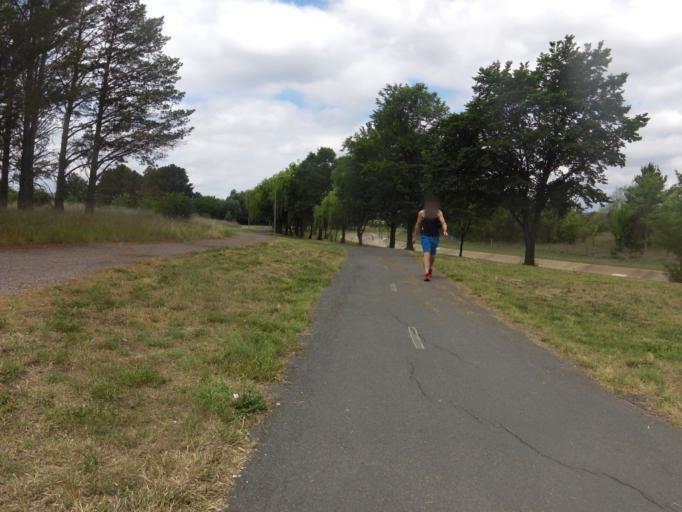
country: AU
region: Australian Capital Territory
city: Macarthur
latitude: -35.4206
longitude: 149.0896
